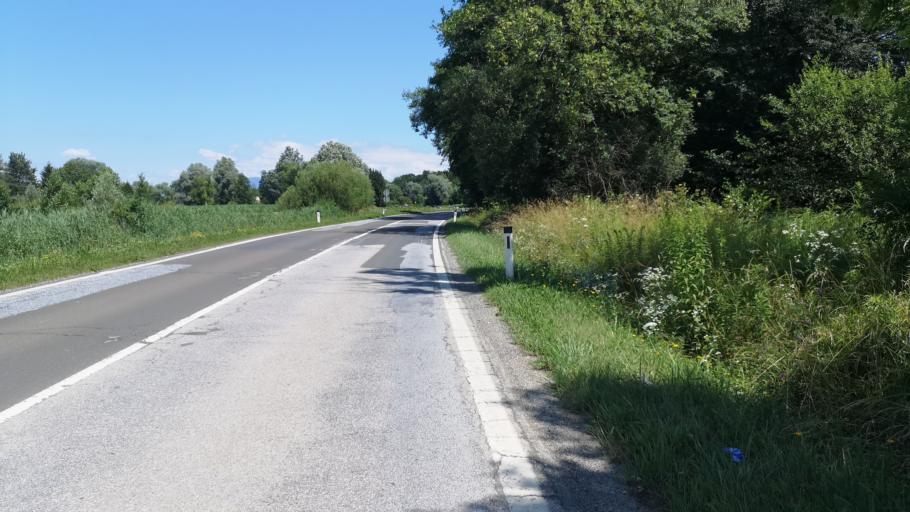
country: AT
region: Styria
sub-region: Politischer Bezirk Graz-Umgebung
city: Mellach
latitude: 46.9524
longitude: 15.5078
